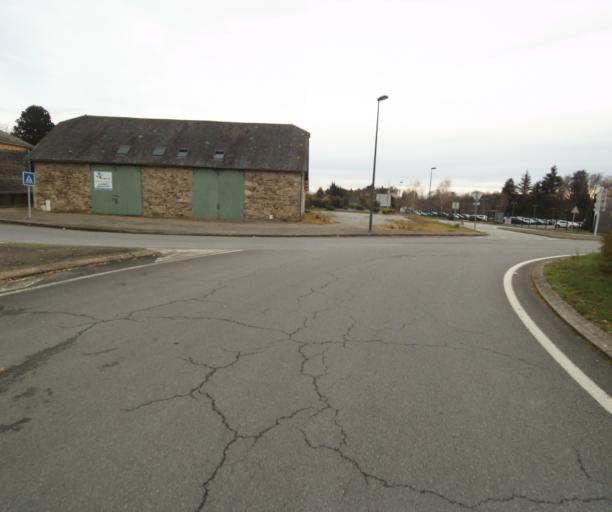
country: FR
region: Limousin
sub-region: Departement de la Correze
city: Saint-Mexant
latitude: 45.2716
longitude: 1.6659
